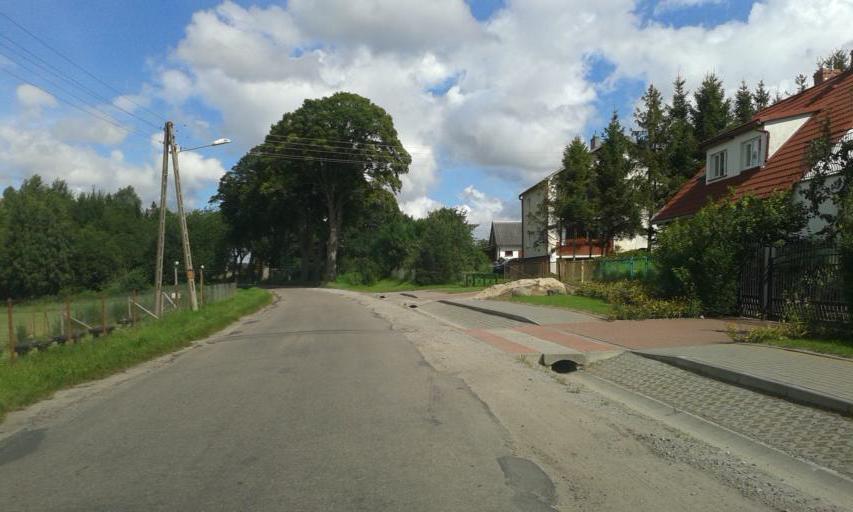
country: PL
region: West Pomeranian Voivodeship
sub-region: Powiat slawienski
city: Slawno
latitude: 54.3061
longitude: 16.6231
